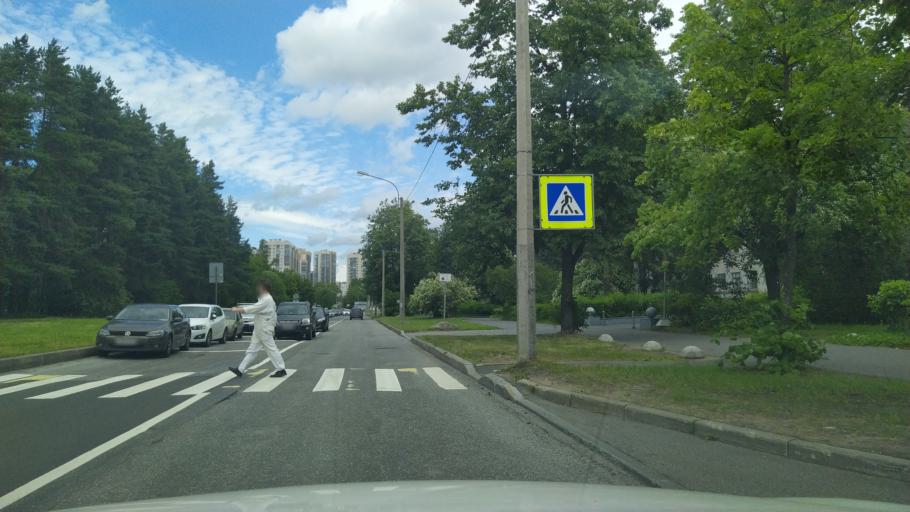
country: RU
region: Leningrad
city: Kalininskiy
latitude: 60.0050
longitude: 30.3839
